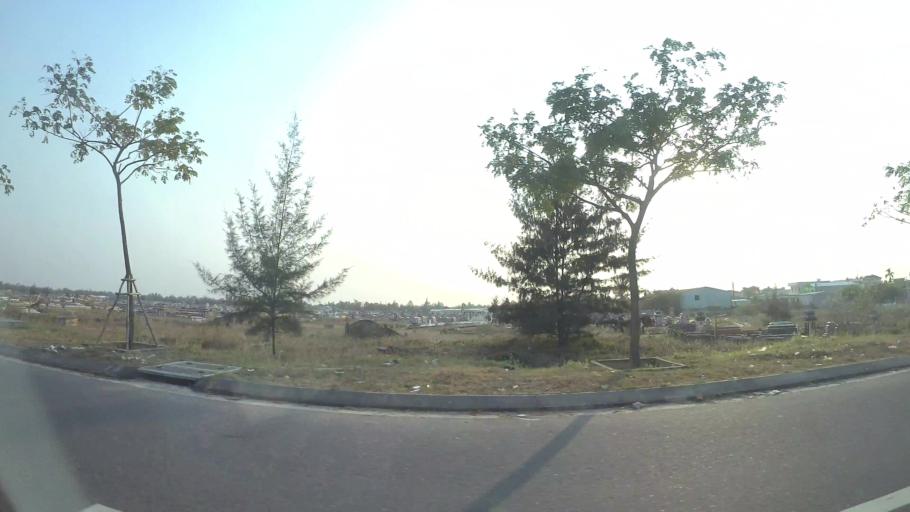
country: VN
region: Da Nang
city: Ngu Hanh Son
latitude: 15.9846
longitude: 108.2420
